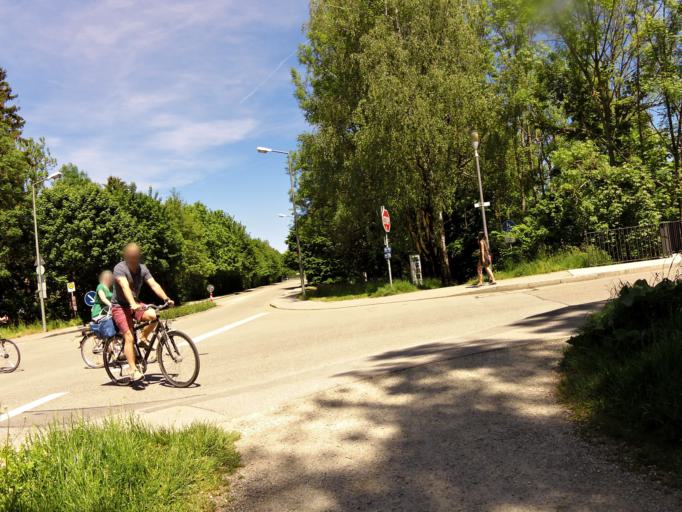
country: DE
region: Bavaria
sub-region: Upper Bavaria
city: Freising
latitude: 48.3978
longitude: 11.7510
